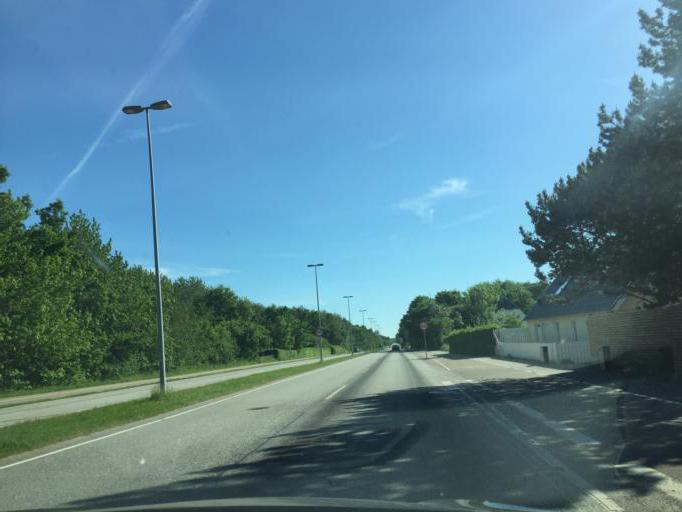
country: DK
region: Zealand
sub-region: Koge Kommune
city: Koge
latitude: 55.4094
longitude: 12.1329
